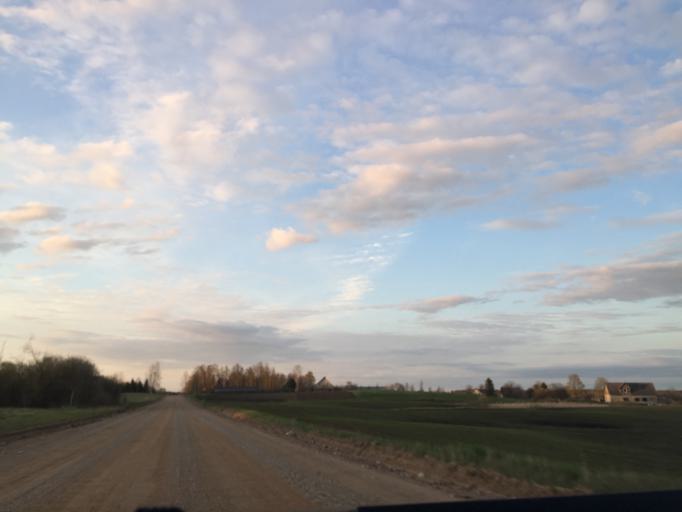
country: LV
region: Gulbenes Rajons
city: Gulbene
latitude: 57.2054
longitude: 26.7790
